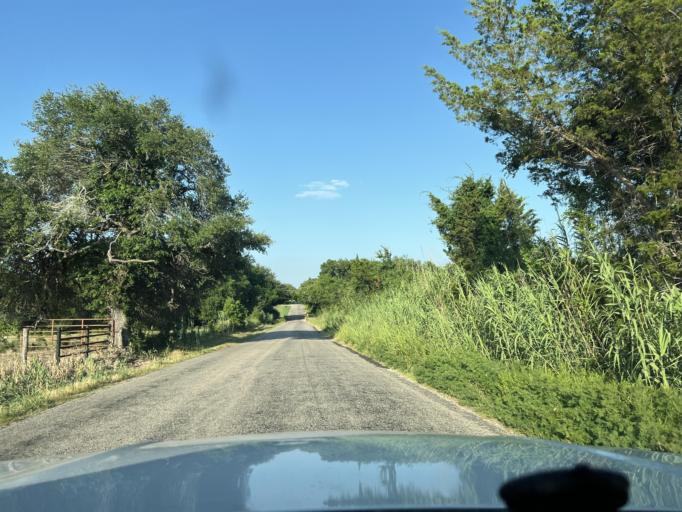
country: US
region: Texas
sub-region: Washington County
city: Brenham
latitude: 30.2296
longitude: -96.3903
